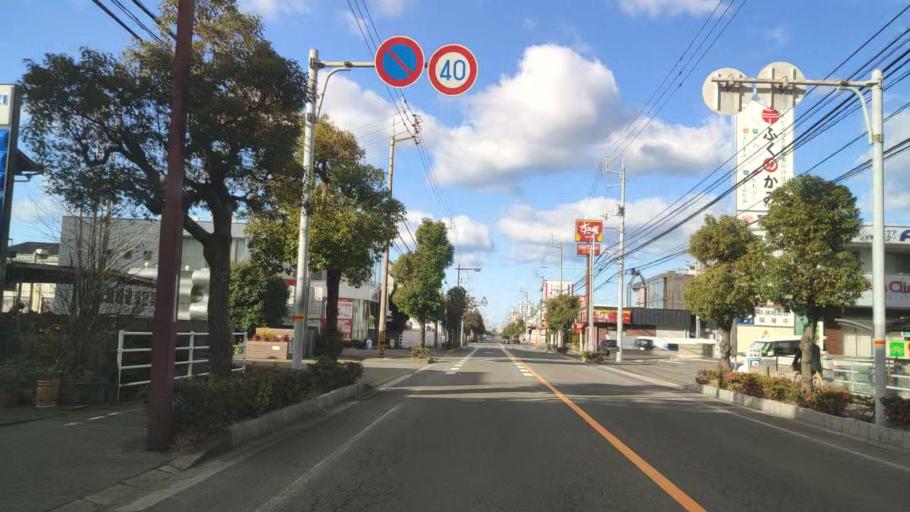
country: JP
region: Ehime
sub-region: Shikoku-chuo Shi
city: Matsuyama
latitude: 33.8284
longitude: 132.7358
